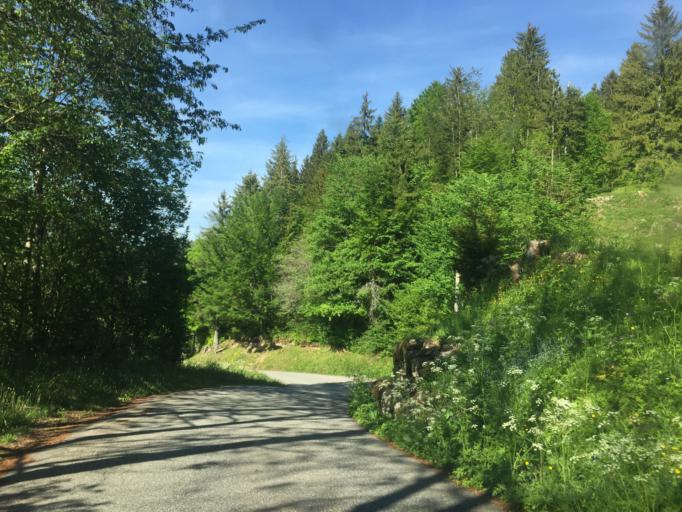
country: FR
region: Rhone-Alpes
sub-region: Departement de l'Isere
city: Barraux
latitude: 45.4552
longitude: 5.8885
